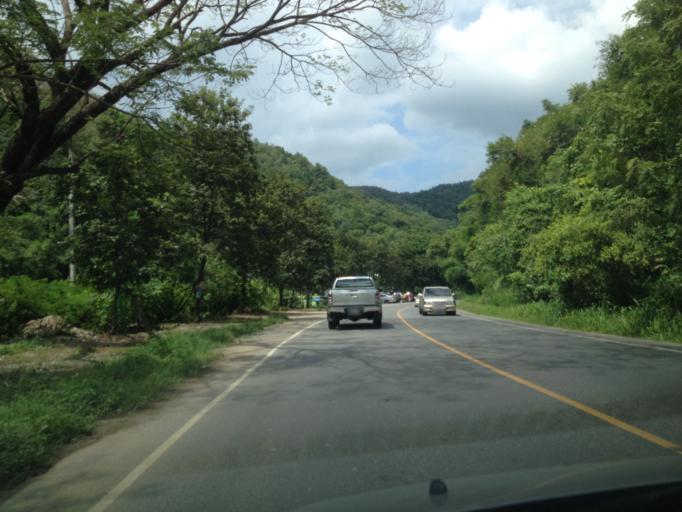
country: TH
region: Chiang Mai
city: Hang Dong
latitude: 18.7367
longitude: 98.8937
